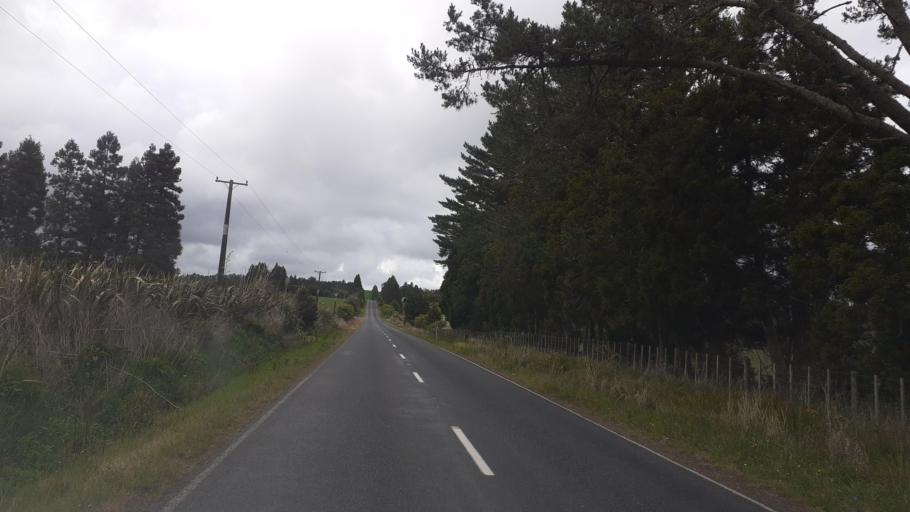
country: NZ
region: Northland
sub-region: Far North District
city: Waimate North
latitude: -35.2587
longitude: 173.8044
